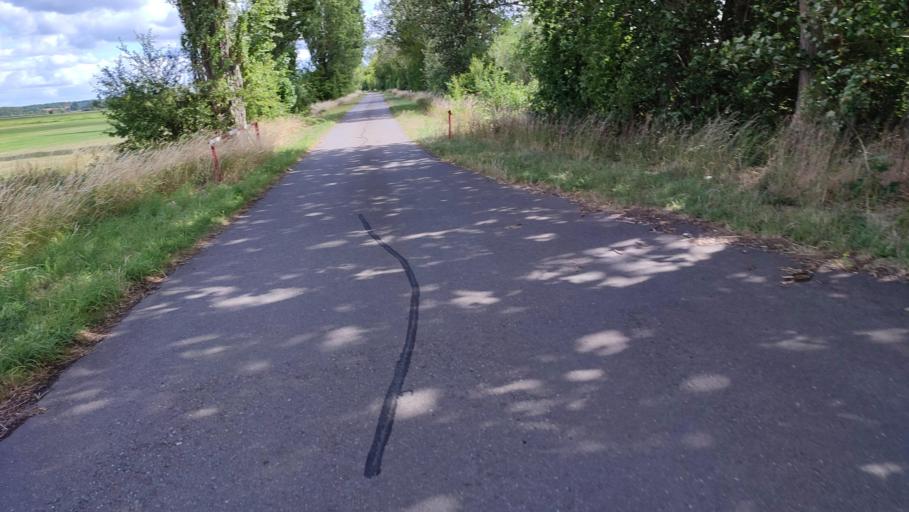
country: DE
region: Lower Saxony
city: Neu Darchau
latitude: 53.2164
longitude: 10.9649
